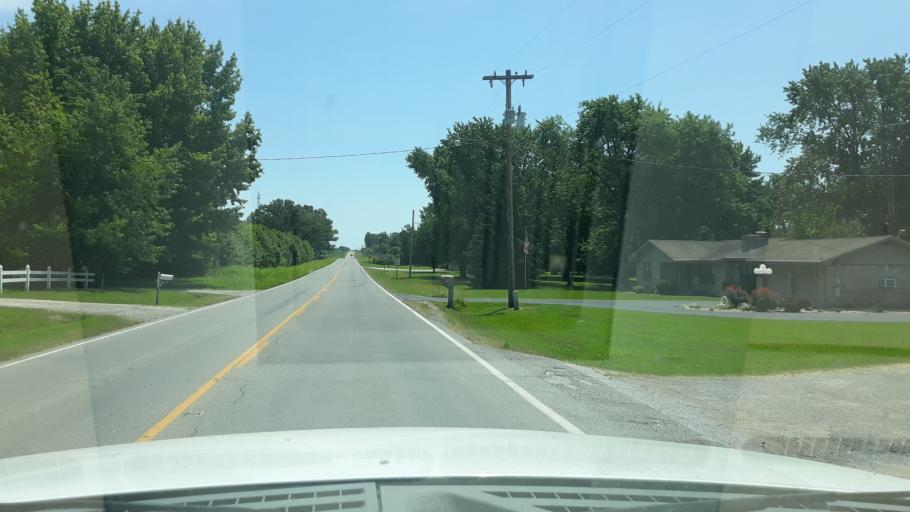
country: US
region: Illinois
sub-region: Saline County
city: Eldorado
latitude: 37.8044
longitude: -88.4363
